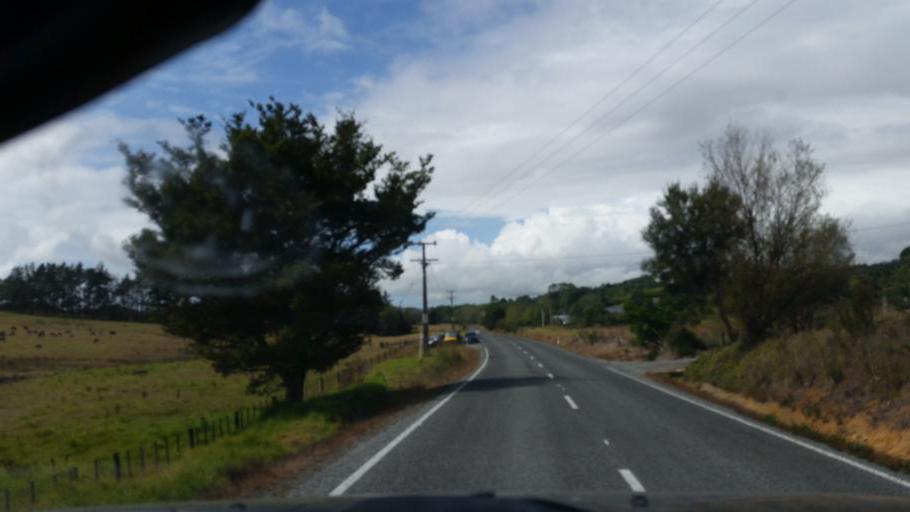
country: NZ
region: Auckland
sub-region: Auckland
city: Wellsford
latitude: -36.1183
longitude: 174.5478
